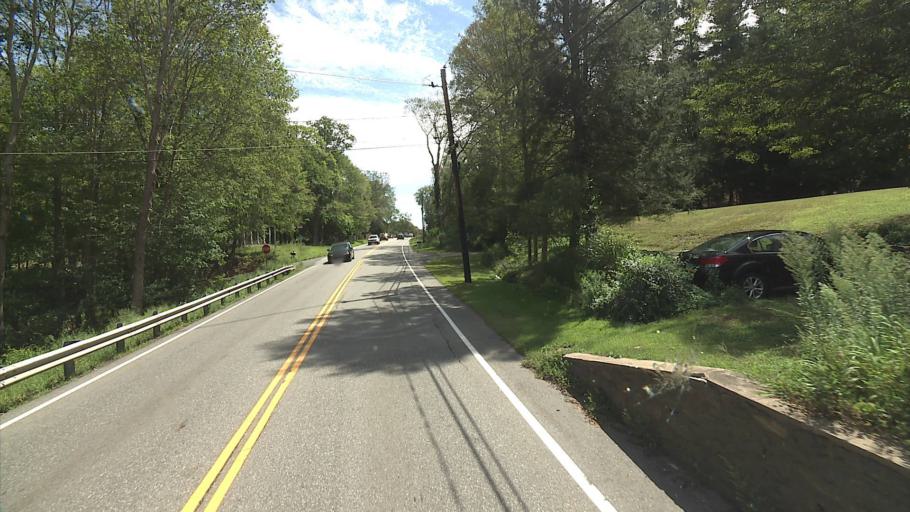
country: US
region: Connecticut
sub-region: Tolland County
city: Mansfield City
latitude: 41.7680
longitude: -72.2004
